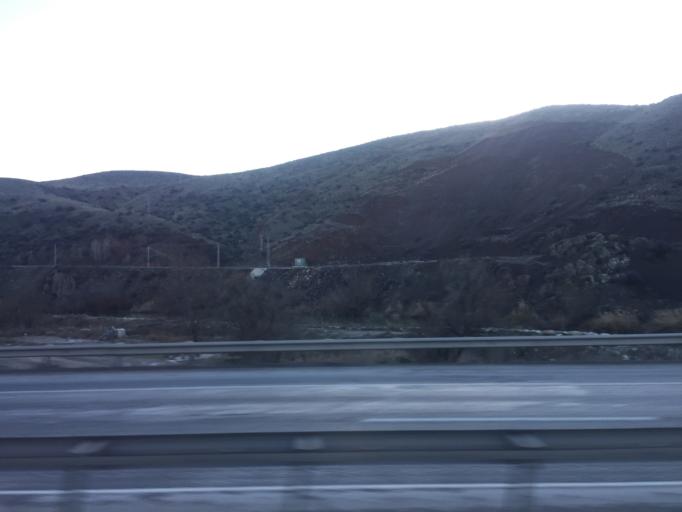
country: TR
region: Kirikkale
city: Yahsihan
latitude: 39.9385
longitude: 33.4141
